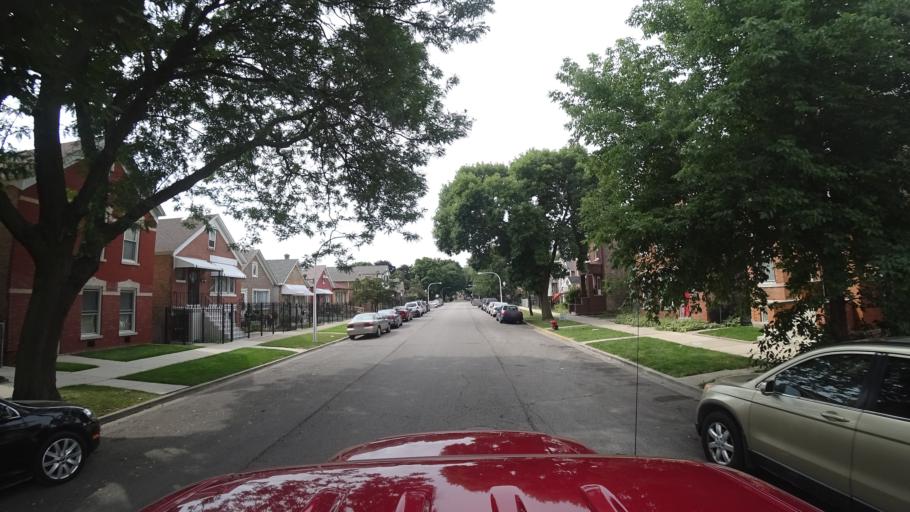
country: US
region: Illinois
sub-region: Cook County
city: Chicago
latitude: 41.8262
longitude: -87.6728
